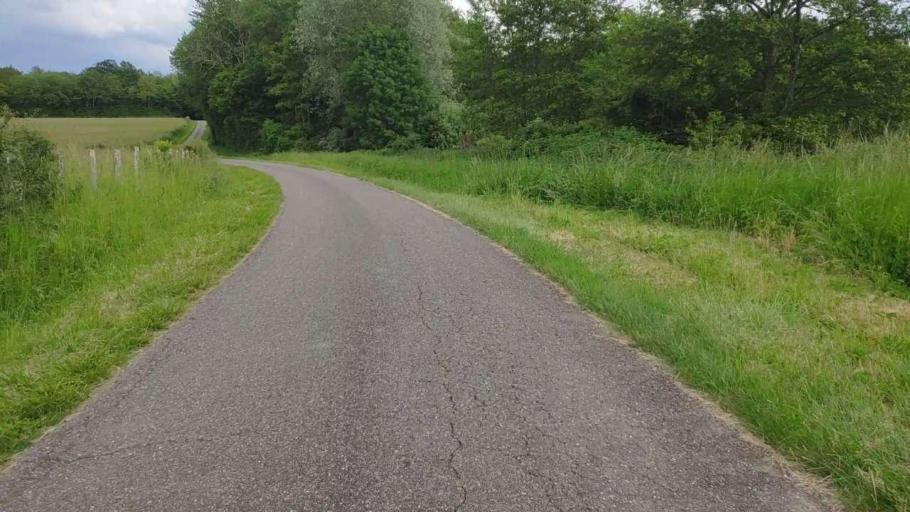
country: FR
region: Bourgogne
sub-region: Departement de Saone-et-Loire
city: Saint-Germain-du-Bois
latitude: 46.7972
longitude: 5.3483
